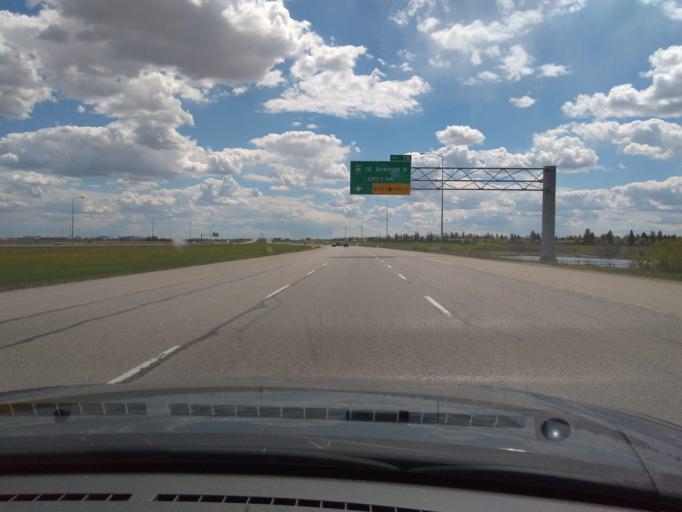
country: CA
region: Alberta
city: Chestermere
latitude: 51.0849
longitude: -113.9207
